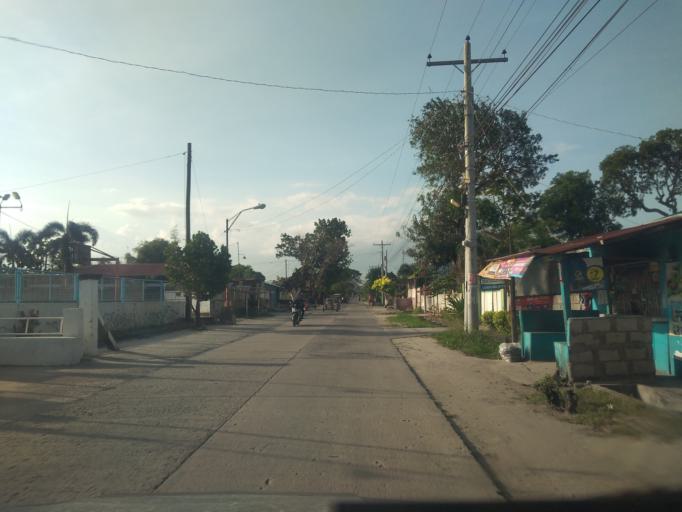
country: PH
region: Central Luzon
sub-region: Province of Pampanga
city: Bulaon
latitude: 15.0915
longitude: 120.6864
